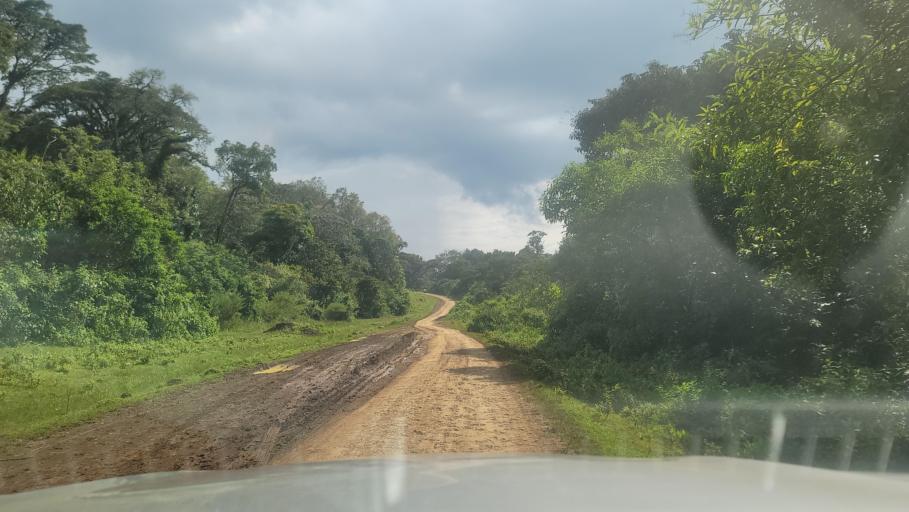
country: ET
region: Oromiya
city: Agaro
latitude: 7.7172
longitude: 36.2585
